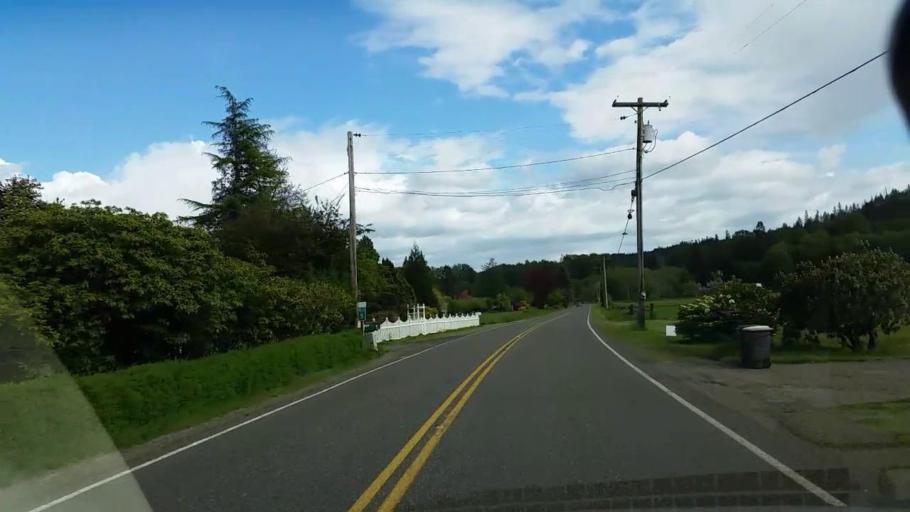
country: US
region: Washington
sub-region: Mason County
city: Shelton
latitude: 47.3193
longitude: -123.2619
